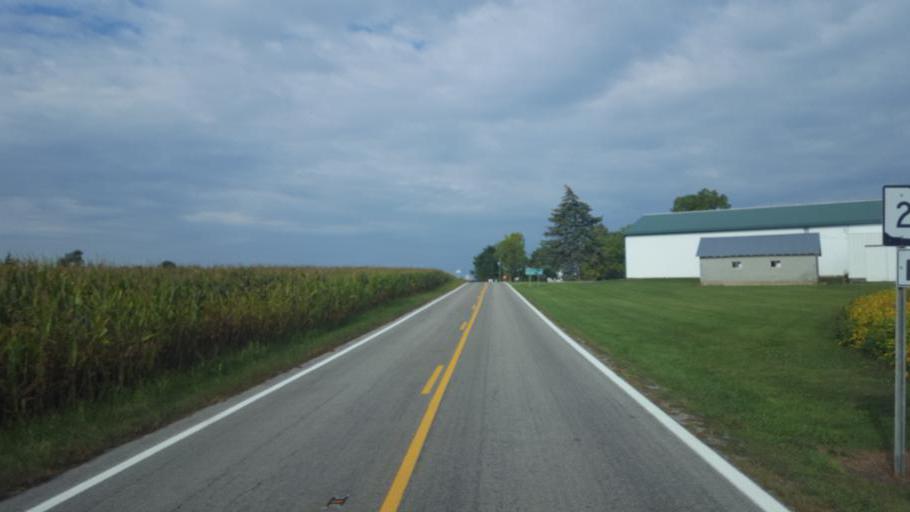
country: US
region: Ohio
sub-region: Marion County
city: Marion
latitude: 40.7173
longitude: -83.1232
